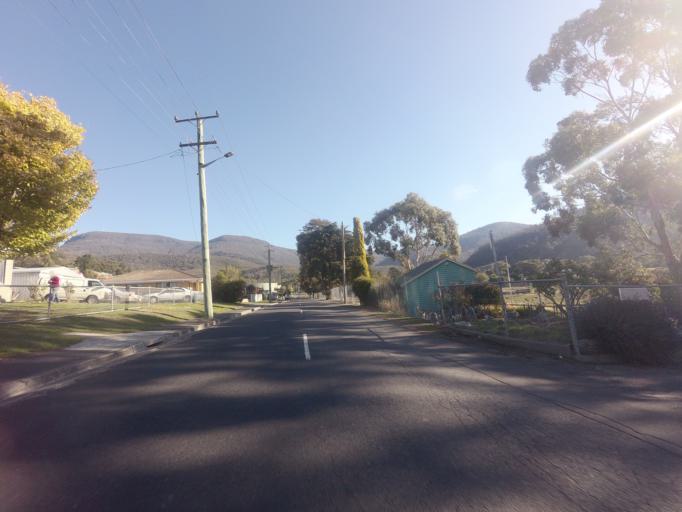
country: AU
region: Tasmania
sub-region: Glenorchy
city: West Moonah
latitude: -42.8512
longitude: 147.2559
